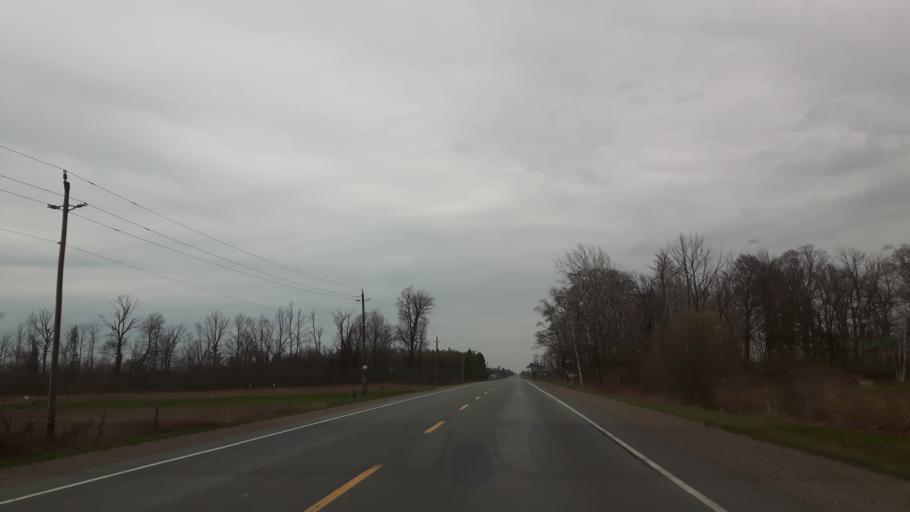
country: CA
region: Ontario
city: Goderich
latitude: 43.5965
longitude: -81.7056
